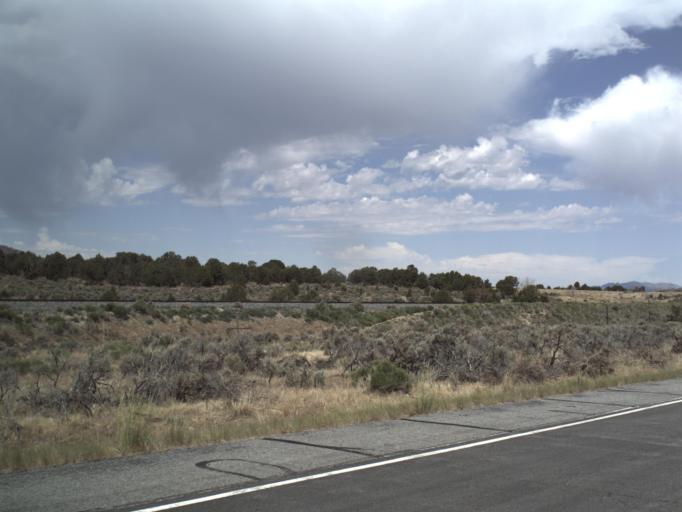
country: US
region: Utah
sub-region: Utah County
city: Genola
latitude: 39.9700
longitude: -112.2559
